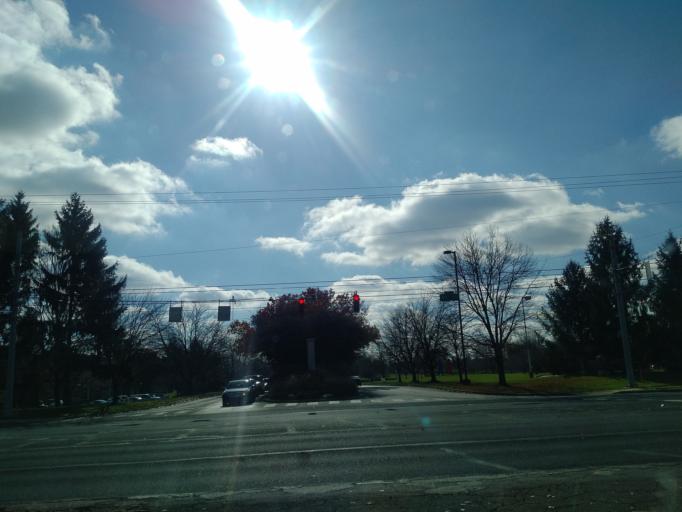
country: US
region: Indiana
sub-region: Marion County
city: Meridian Hills
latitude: 39.9127
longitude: -86.1233
